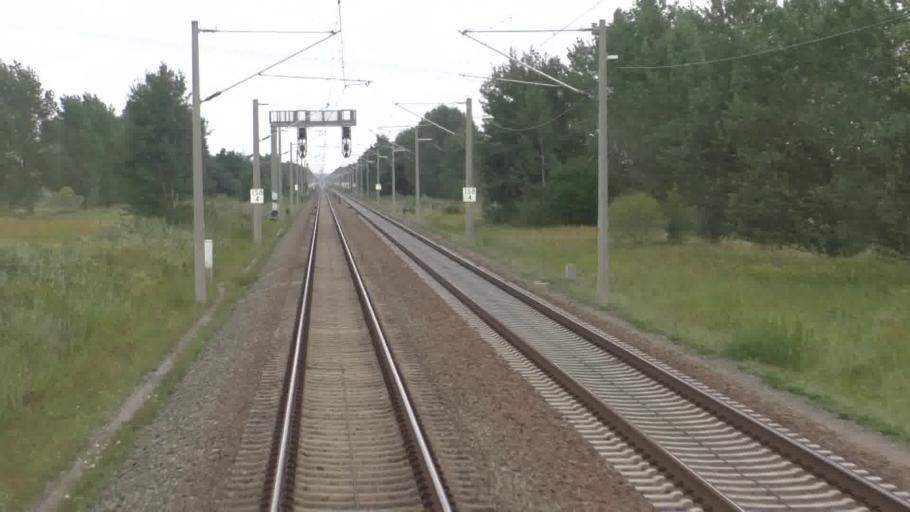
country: DE
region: Brandenburg
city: Nennhausen
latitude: 52.5979
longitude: 12.5361
